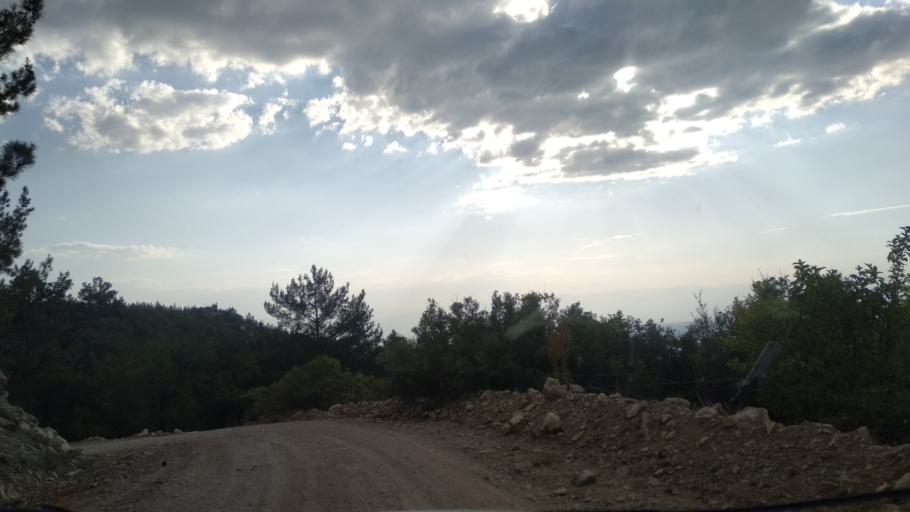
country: TR
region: Mersin
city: Sarikavak
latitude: 36.5891
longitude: 33.6751
